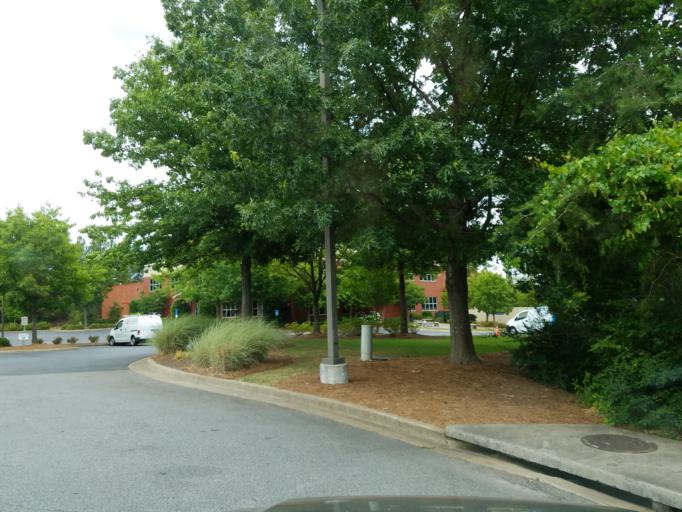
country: US
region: Georgia
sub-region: Cobb County
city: Smyrna
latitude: 33.9166
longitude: -84.4912
